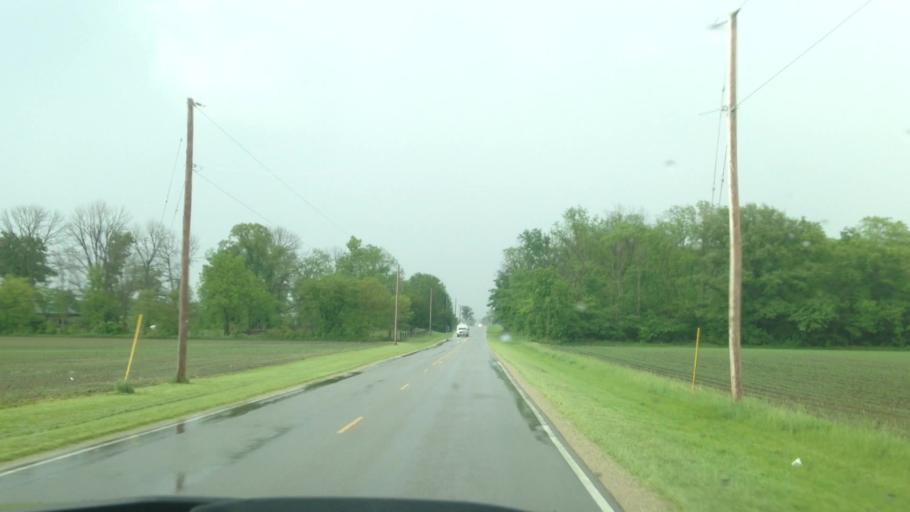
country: US
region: Ohio
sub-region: Darke County
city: Greenville
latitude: 40.1505
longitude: -84.6582
